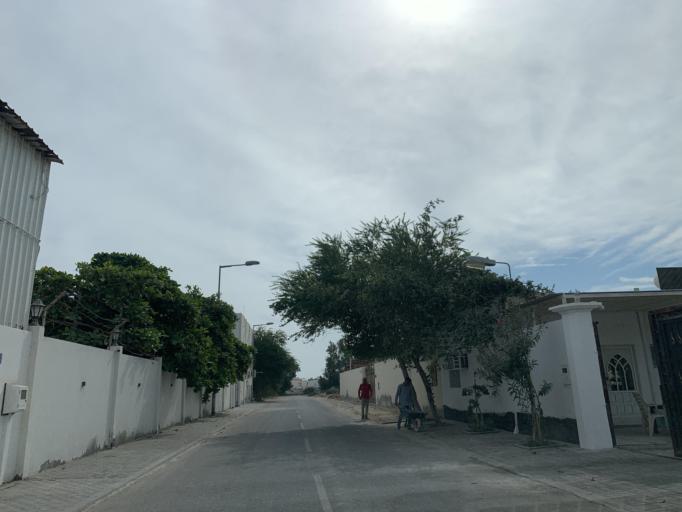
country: BH
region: Central Governorate
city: Madinat Hamad
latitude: 26.1134
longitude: 50.4728
